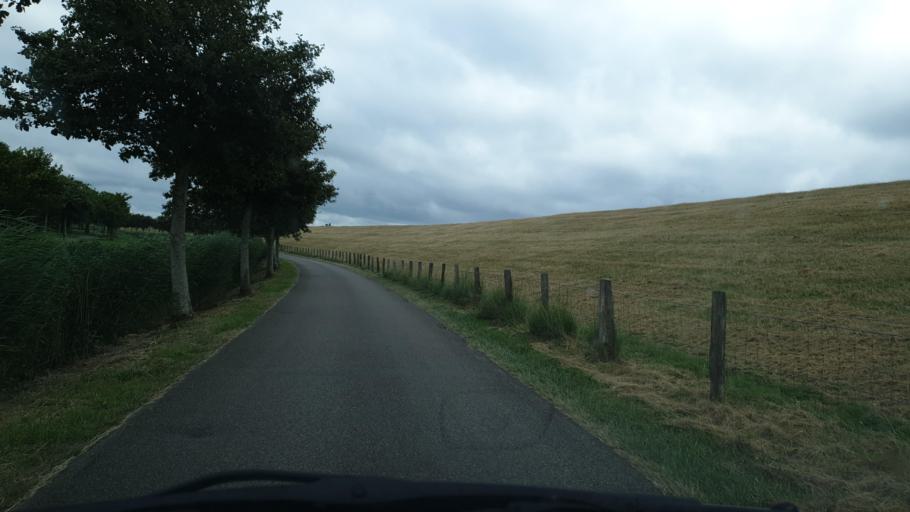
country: DE
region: Schleswig-Holstein
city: Friedrichskoog
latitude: 54.0265
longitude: 8.8386
